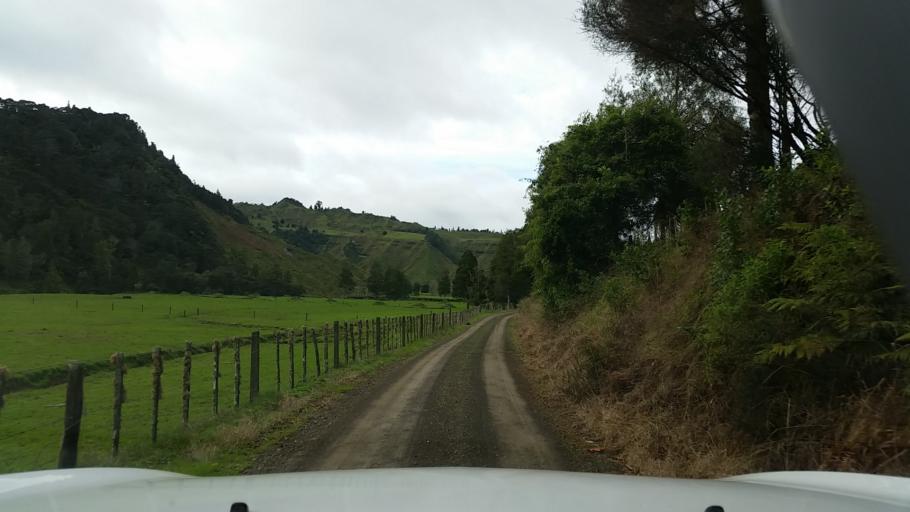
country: NZ
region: Taranaki
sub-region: New Plymouth District
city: Waitara
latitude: -38.7542
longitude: 174.6976
